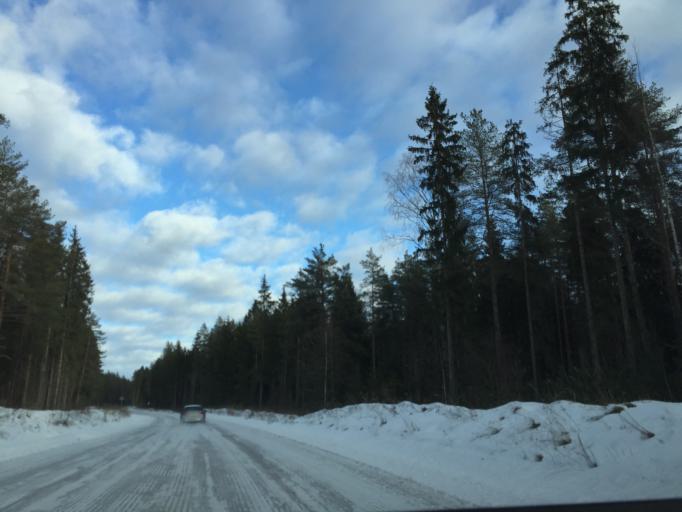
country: LV
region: Ogre
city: Jumprava
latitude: 56.5708
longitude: 24.9349
